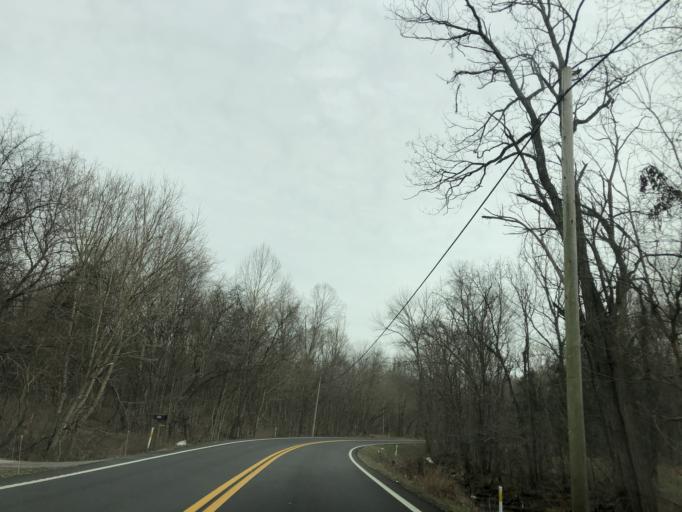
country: US
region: Tennessee
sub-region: Robertson County
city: Greenbrier
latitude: 36.4766
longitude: -86.7633
